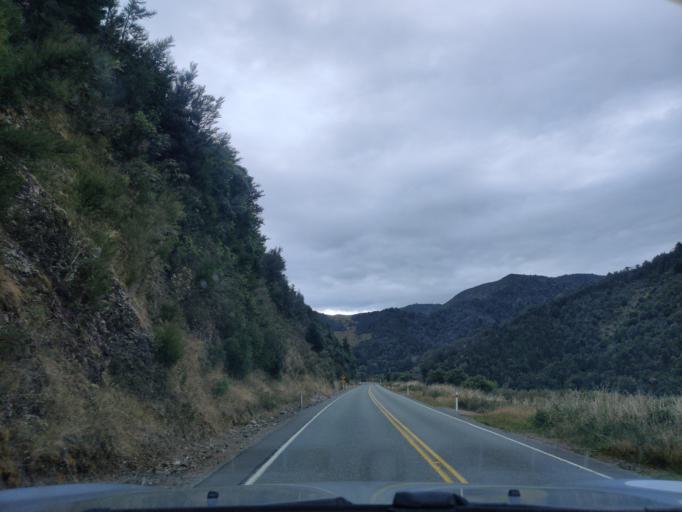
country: NZ
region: Tasman
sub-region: Tasman District
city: Wakefield
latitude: -41.6975
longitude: 172.6211
